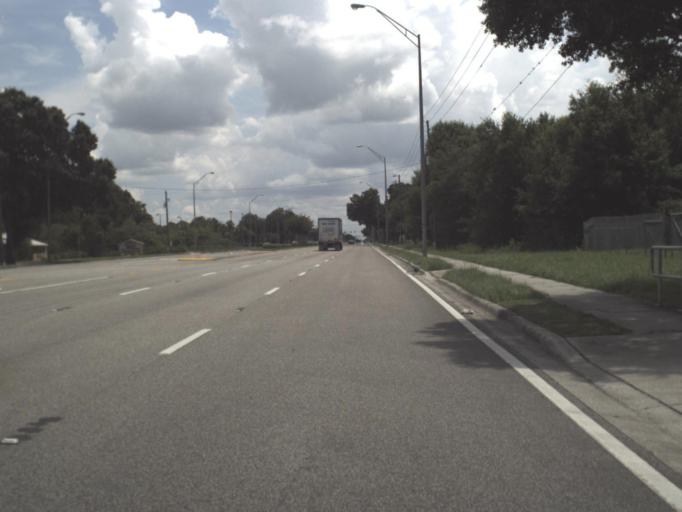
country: US
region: Florida
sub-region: Hillsborough County
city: Plant City
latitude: 28.0309
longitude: -82.1051
